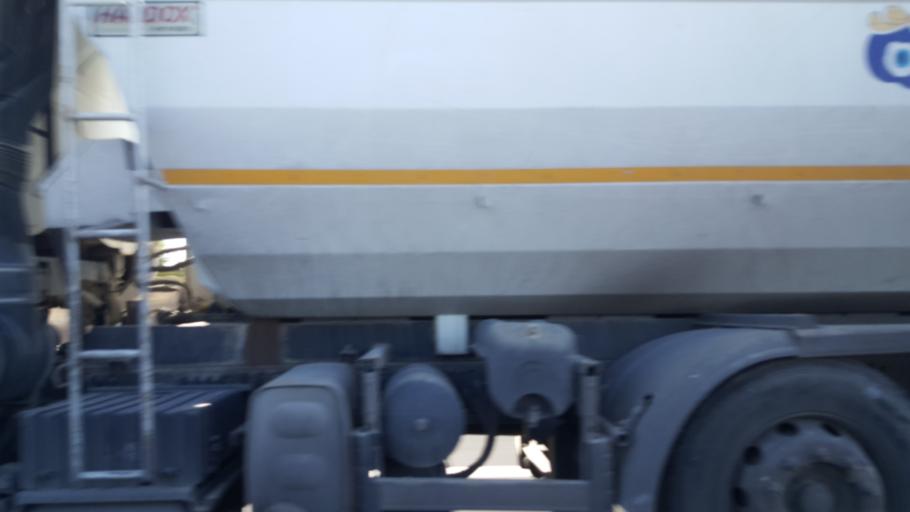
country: TR
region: Ankara
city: Mamak
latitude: 39.9026
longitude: 32.9921
